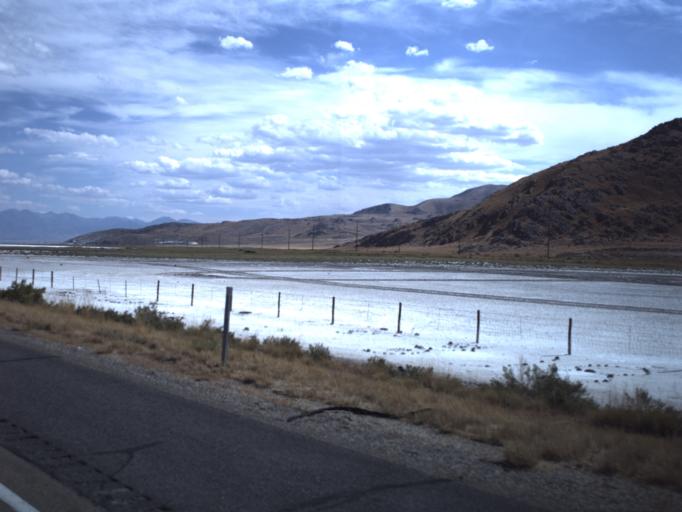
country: US
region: Utah
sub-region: Tooele County
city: Grantsville
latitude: 40.7408
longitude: -112.6264
